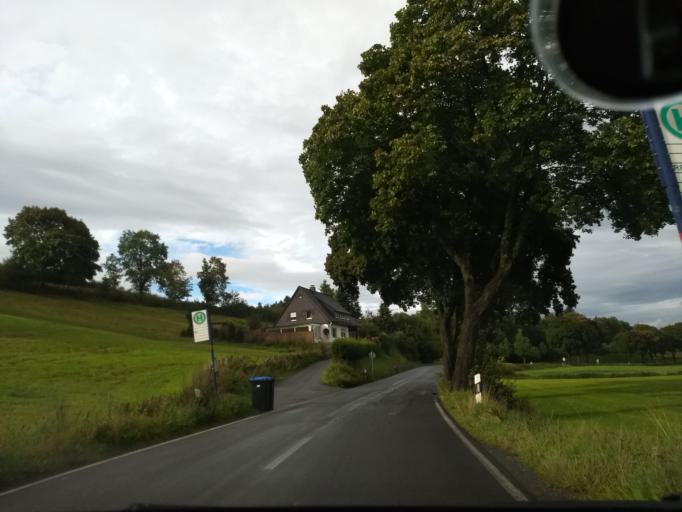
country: DE
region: North Rhine-Westphalia
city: Eslohe
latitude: 51.2387
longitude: 8.1339
